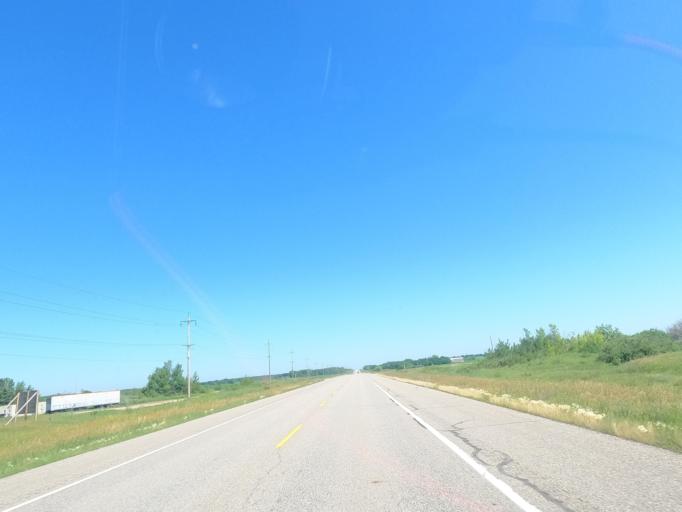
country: CA
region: Manitoba
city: Brandon
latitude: 49.6044
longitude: -99.9615
